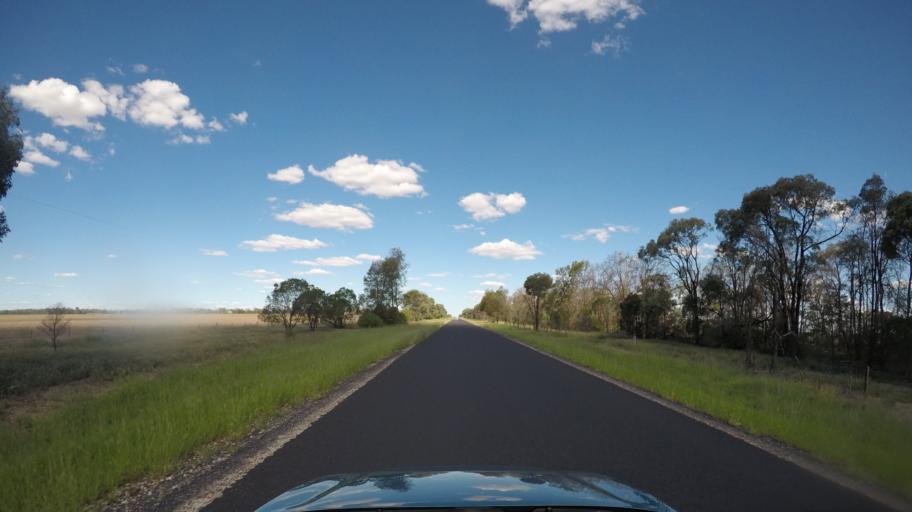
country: AU
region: Queensland
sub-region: Goondiwindi
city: Goondiwindi
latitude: -28.1660
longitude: 150.1778
